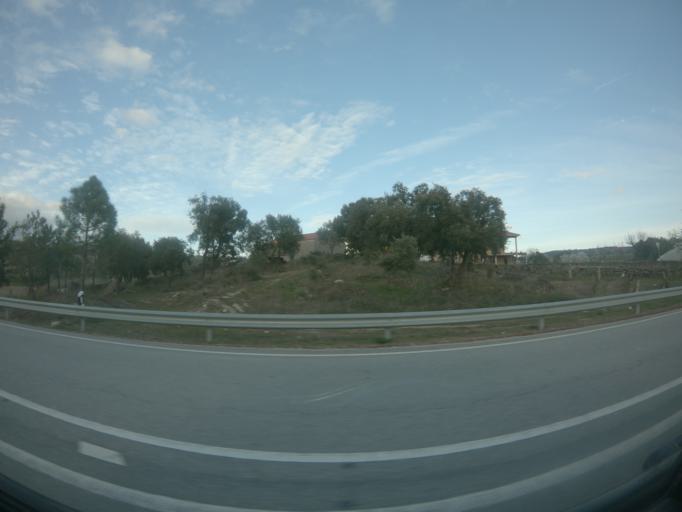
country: PT
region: Braganca
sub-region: Carrazeda de Ansiaes
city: Carrazeda de Anciaes
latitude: 41.2749
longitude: -7.3270
